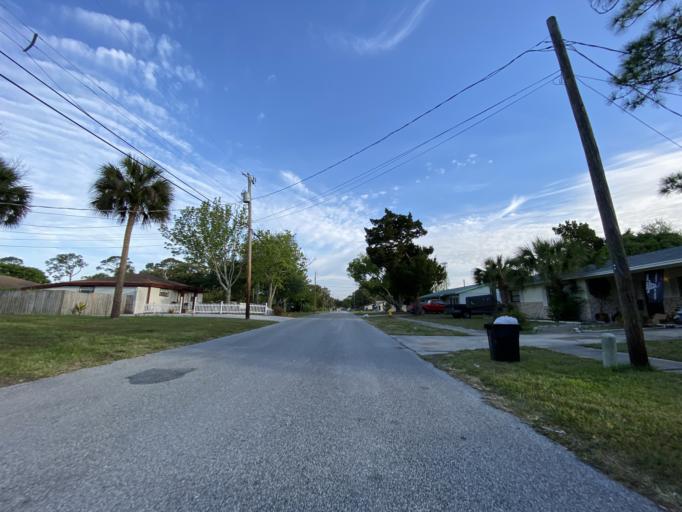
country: US
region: Florida
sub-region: Volusia County
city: South Daytona
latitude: 29.1755
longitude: -81.0090
